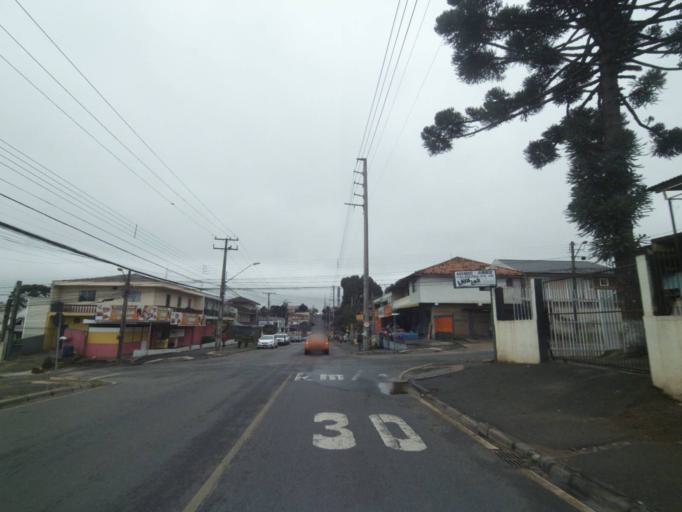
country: BR
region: Parana
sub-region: Curitiba
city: Curitiba
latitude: -25.5088
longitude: -49.3045
